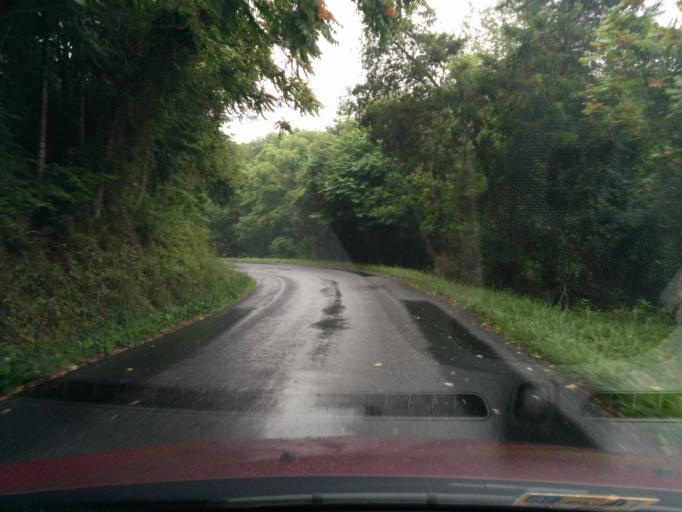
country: US
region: Virginia
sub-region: Rockbridge County
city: East Lexington
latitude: 37.8499
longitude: -79.4247
